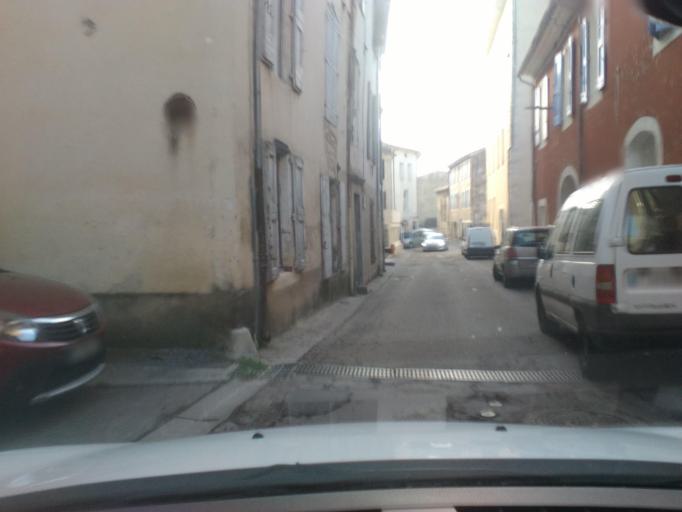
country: FR
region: Languedoc-Roussillon
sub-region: Departement du Gard
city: Lasalle
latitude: 44.0477
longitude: 3.8487
